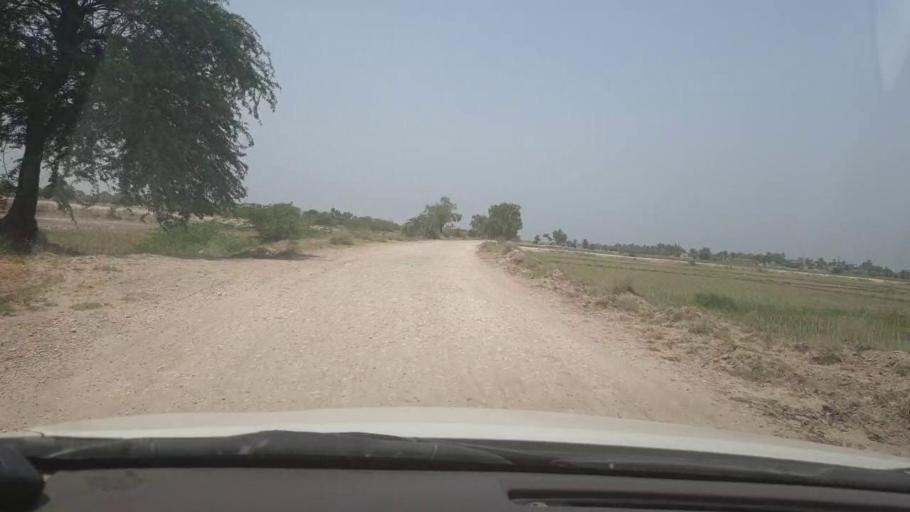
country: PK
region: Sindh
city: Shikarpur
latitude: 27.9413
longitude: 68.5732
